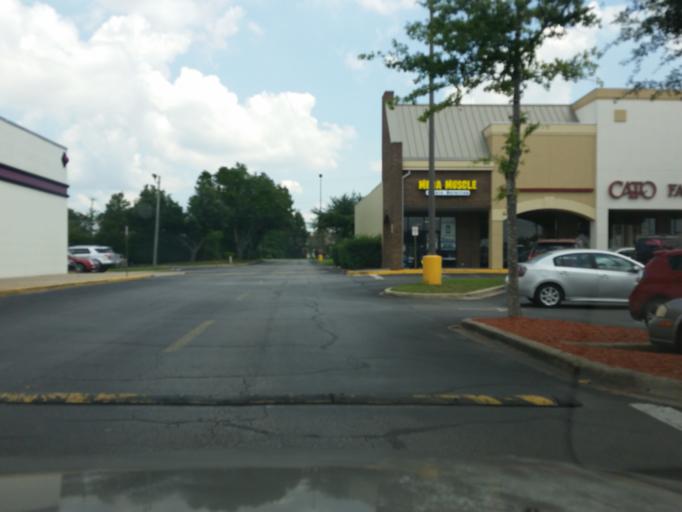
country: US
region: Florida
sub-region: Escambia County
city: Brent
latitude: 30.4901
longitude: -87.2254
